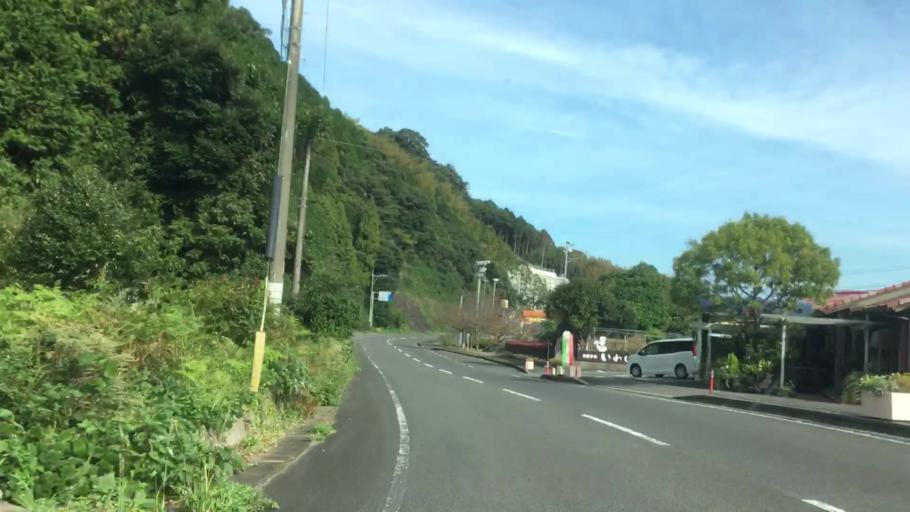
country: JP
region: Nagasaki
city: Sasebo
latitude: 32.9914
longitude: 129.6517
